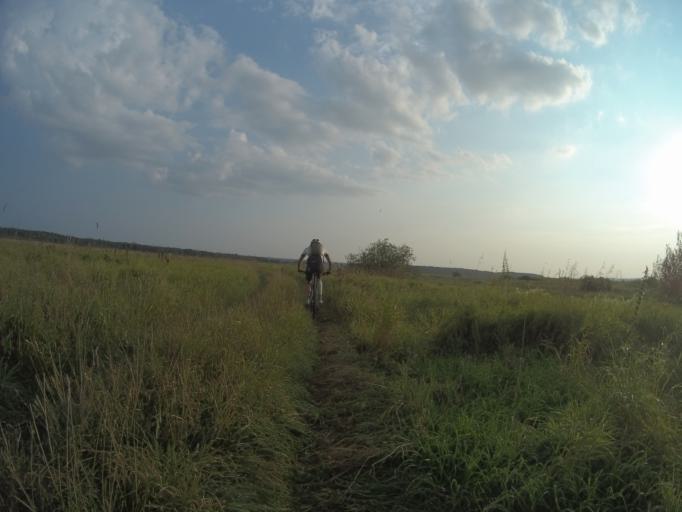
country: RU
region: Vladimir
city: Orgtrud
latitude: 56.3039
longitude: 40.6314
